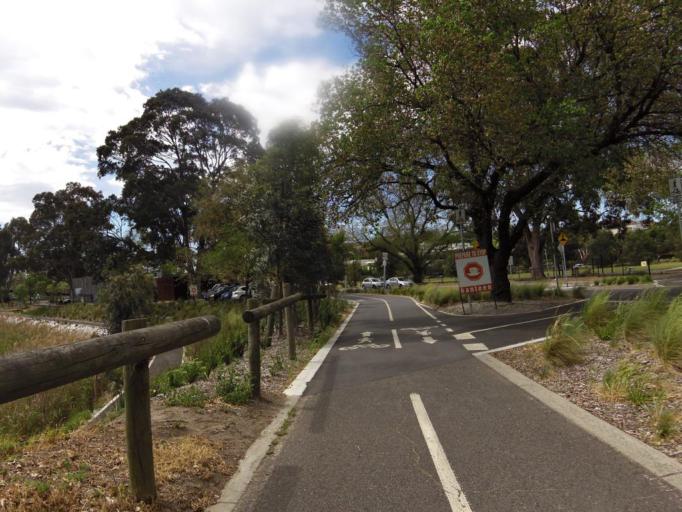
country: AU
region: Victoria
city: Albert Park
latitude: -37.8346
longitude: 145.0044
